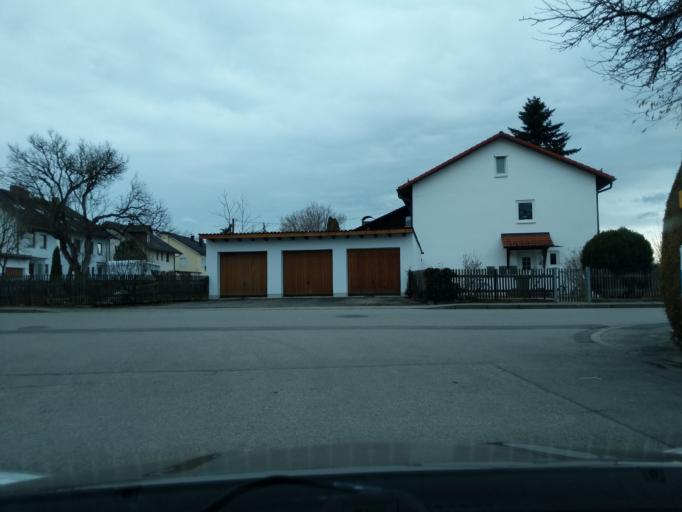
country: DE
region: Bavaria
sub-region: Upper Bavaria
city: Grafing bei Munchen
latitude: 48.0501
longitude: 11.9599
